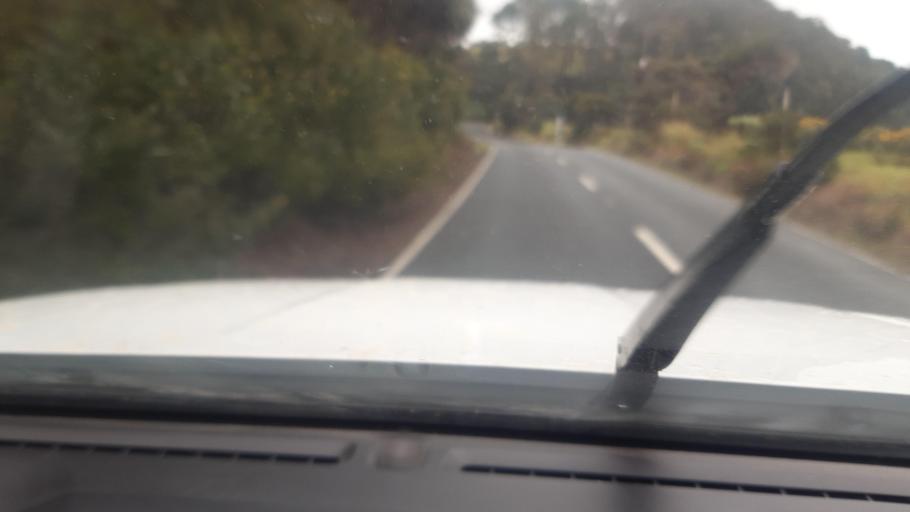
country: NZ
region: Northland
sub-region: Far North District
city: Kaitaia
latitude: -34.9997
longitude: 173.2158
